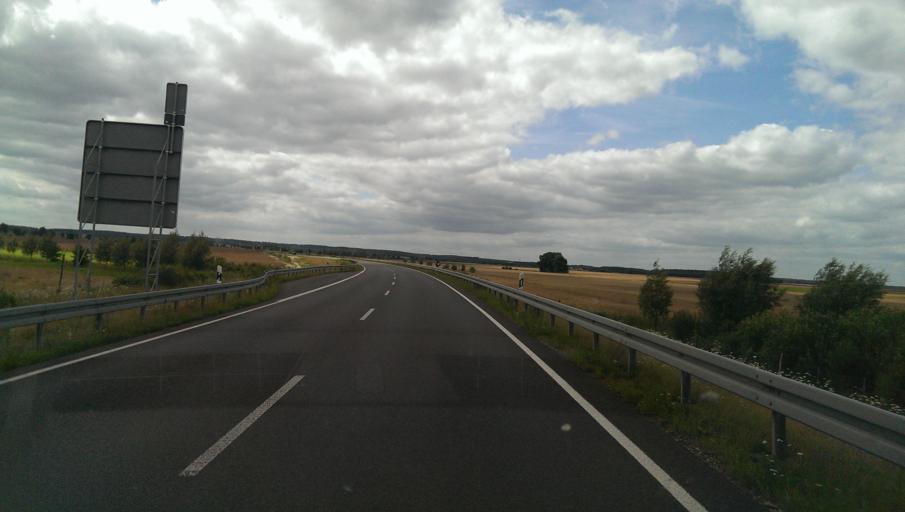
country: DE
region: Brandenburg
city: Niemegk
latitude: 52.1074
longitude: 12.6715
